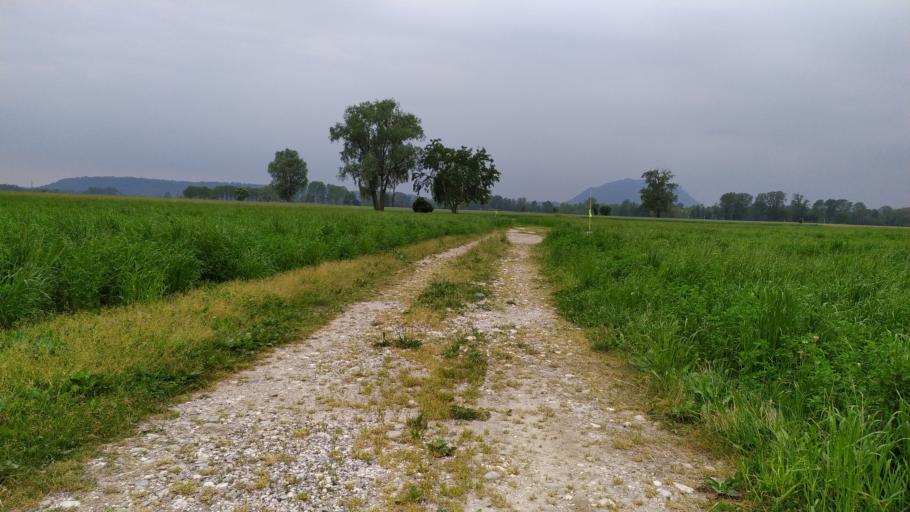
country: IT
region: Friuli Venezia Giulia
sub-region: Provincia di Udine
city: Osoppo
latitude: 46.2336
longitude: 13.0644
